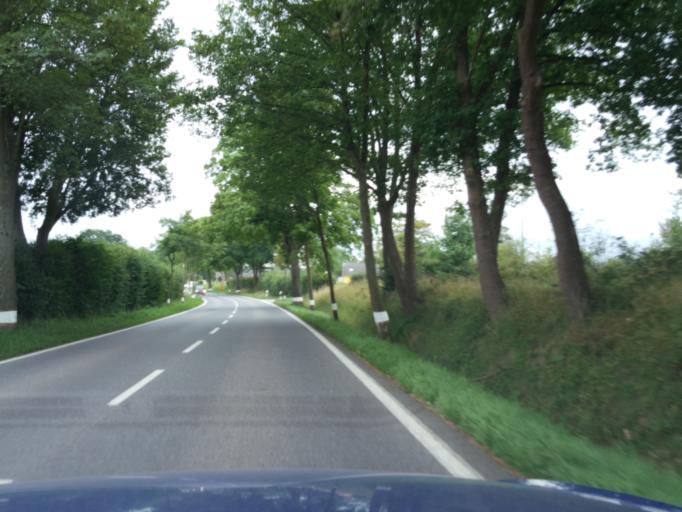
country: LU
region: Luxembourg
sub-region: Canton de Capellen
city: Kehlen
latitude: 49.6742
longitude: 6.0386
